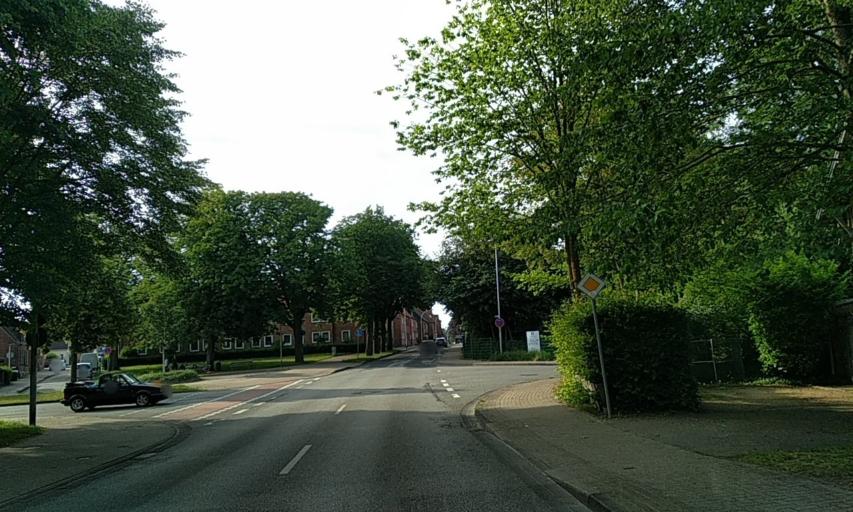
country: DE
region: Schleswig-Holstein
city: Schleswig
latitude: 54.5230
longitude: 9.5622
